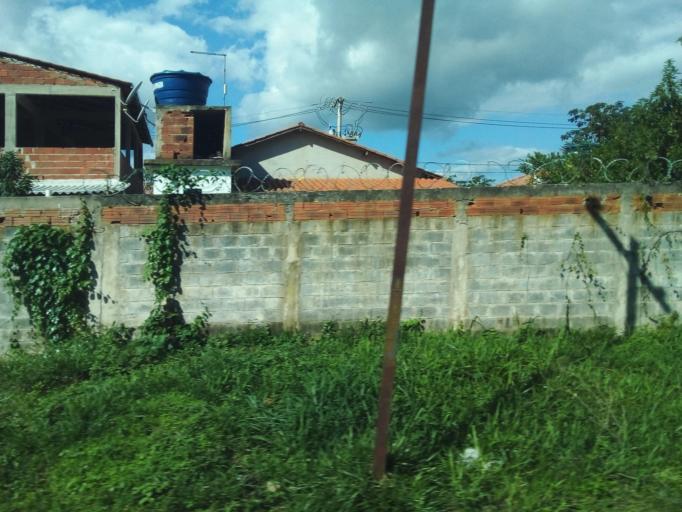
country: BR
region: Minas Gerais
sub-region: Divino Das Laranjeiras
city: Divino das Laranjeiras
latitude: -18.9771
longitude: -41.6539
